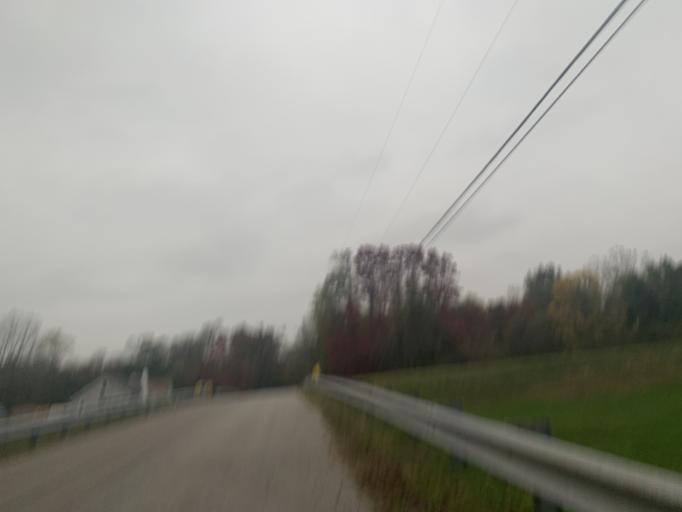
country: US
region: Kentucky
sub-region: Jefferson County
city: Saint Dennis
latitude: 38.2070
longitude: -85.8562
